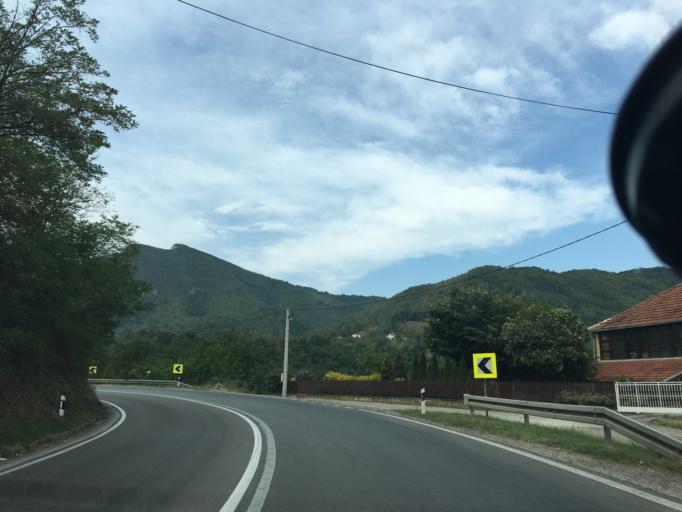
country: RS
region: Central Serbia
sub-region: Moravicki Okrug
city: Lucani
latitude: 43.9188
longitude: 20.2237
